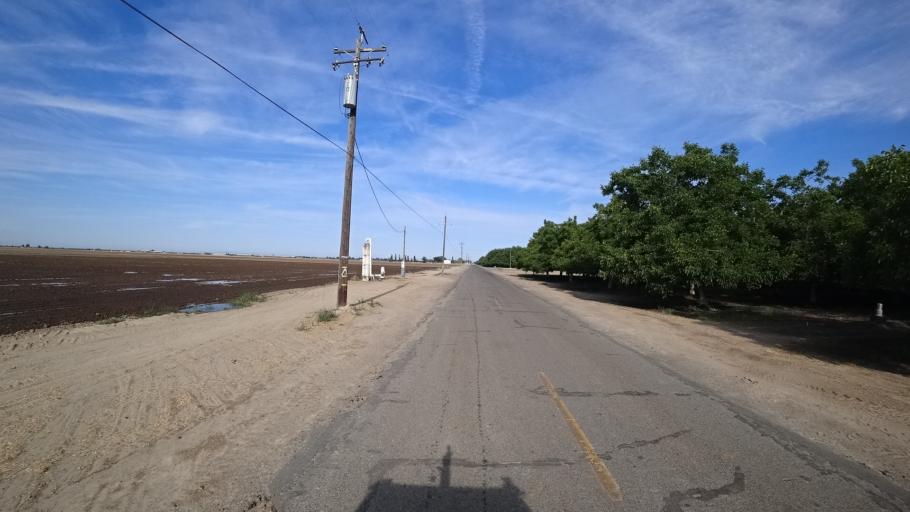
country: US
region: California
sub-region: Fresno County
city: Kingsburg
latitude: 36.4160
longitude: -119.5447
